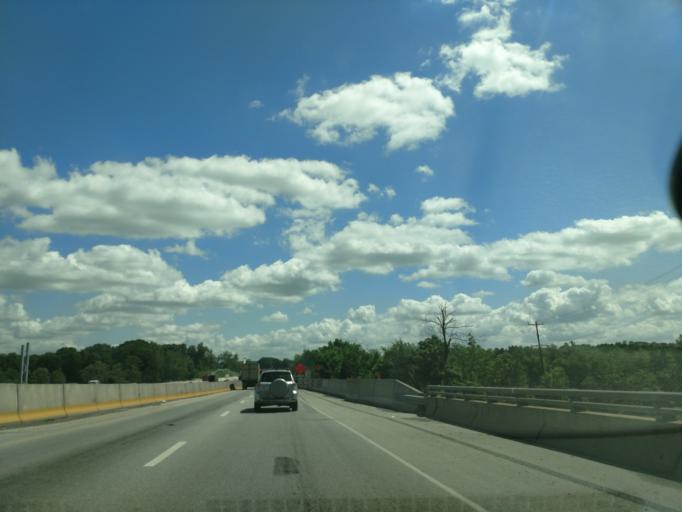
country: US
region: Pennsylvania
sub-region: Montgomery County
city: Audubon
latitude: 40.1103
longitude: -75.4202
